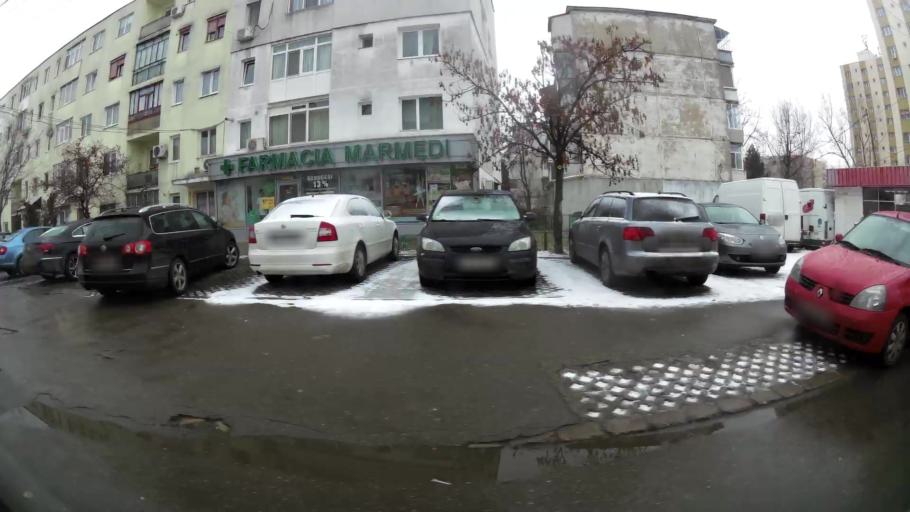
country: RO
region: Prahova
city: Ploiesti
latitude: 44.9478
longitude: 25.9976
